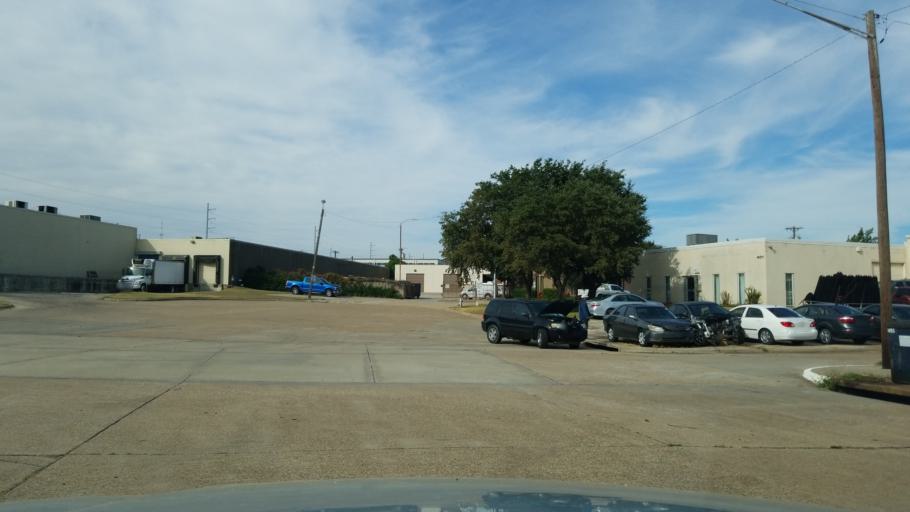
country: US
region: Texas
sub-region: Dallas County
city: Garland
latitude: 32.9106
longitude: -96.6679
